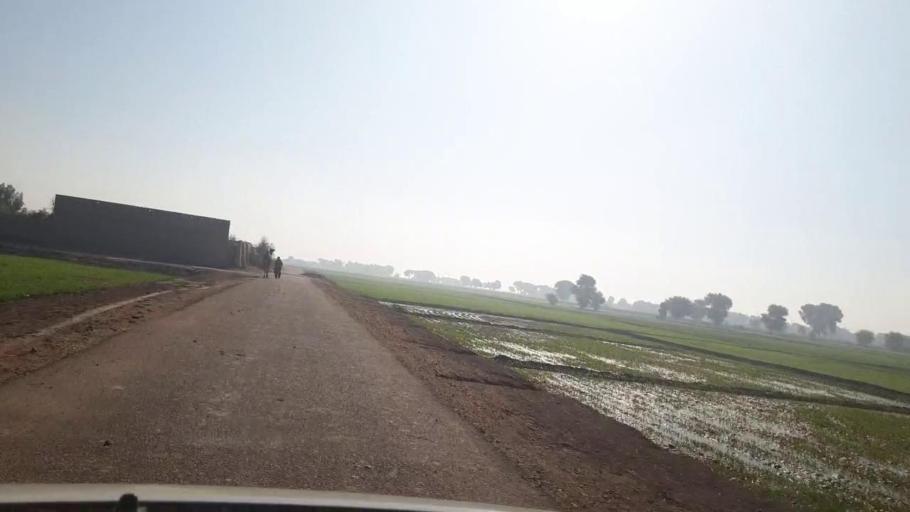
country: PK
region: Sindh
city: Dadu
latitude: 26.6398
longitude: 67.8294
